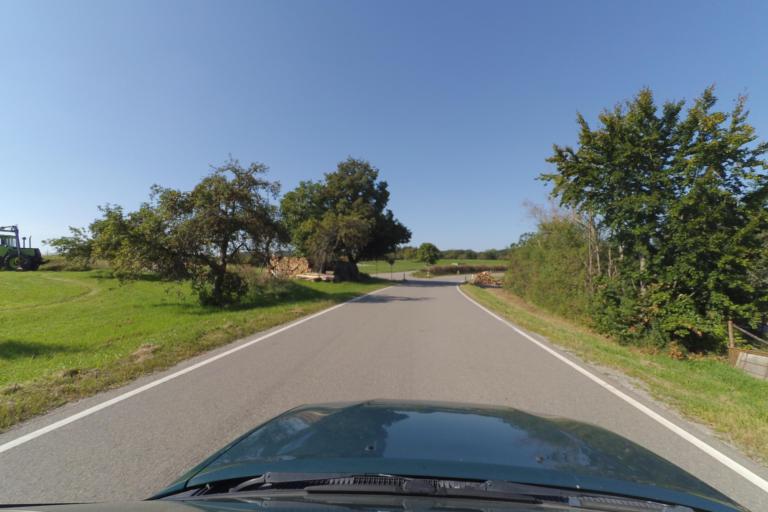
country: DE
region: Baden-Wuerttemberg
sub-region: Regierungsbezirk Stuttgart
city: Lowenstein
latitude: 49.0514
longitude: 9.4033
